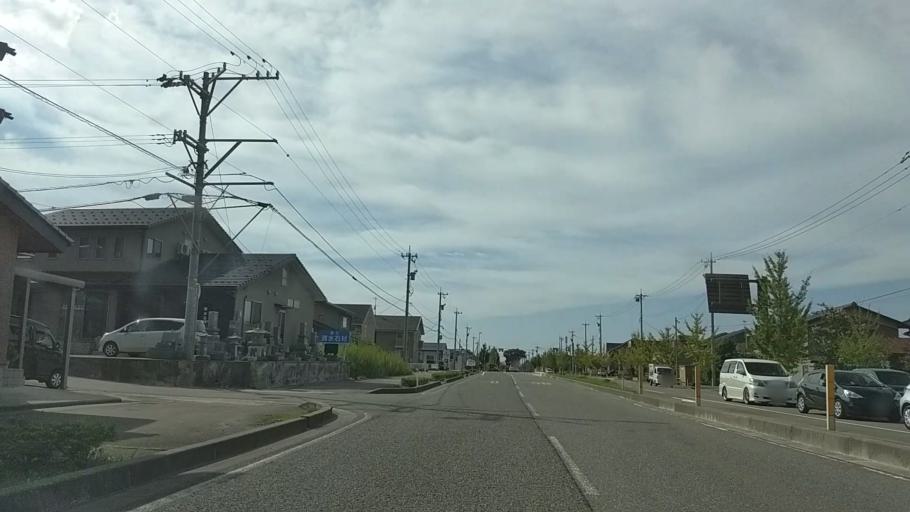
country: JP
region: Ishikawa
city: Nonoichi
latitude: 36.5342
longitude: 136.6645
